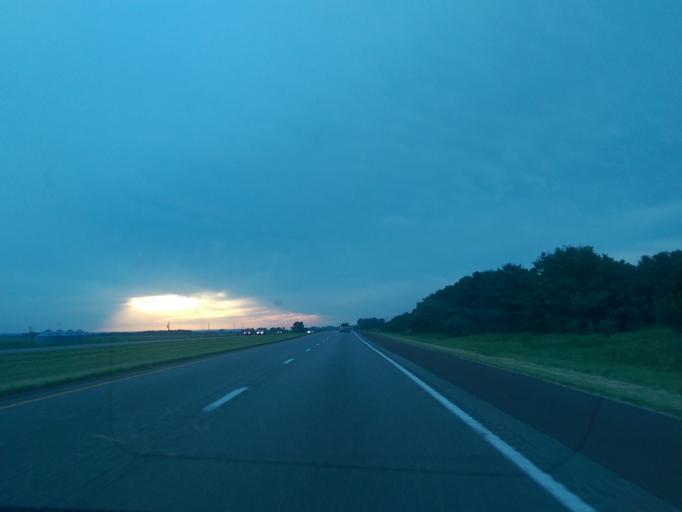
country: US
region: Missouri
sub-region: Holt County
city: Mound City
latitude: 40.1615
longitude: -95.2805
